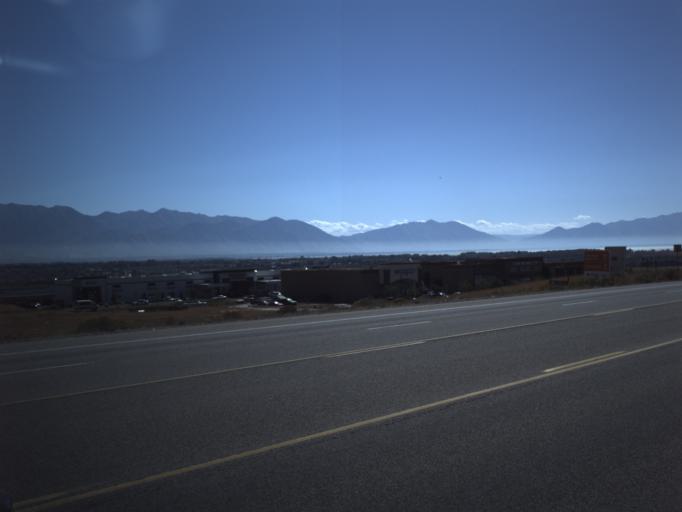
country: US
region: Utah
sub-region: Utah County
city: Saratoga Springs
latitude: 40.4033
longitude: -111.9205
